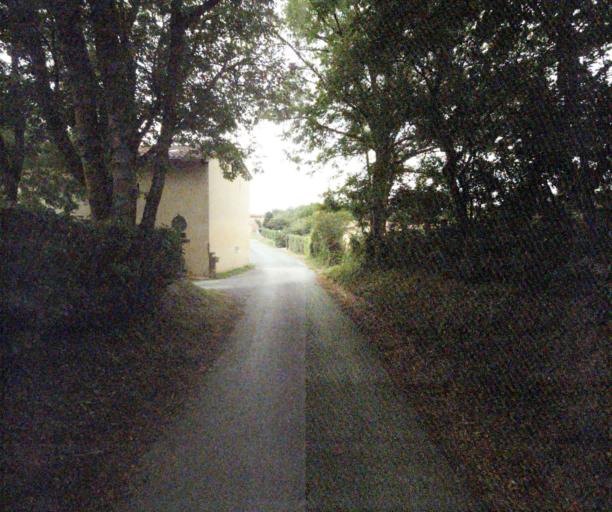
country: FR
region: Midi-Pyrenees
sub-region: Departement du Tarn
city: Soreze
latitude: 43.4489
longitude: 2.0648
